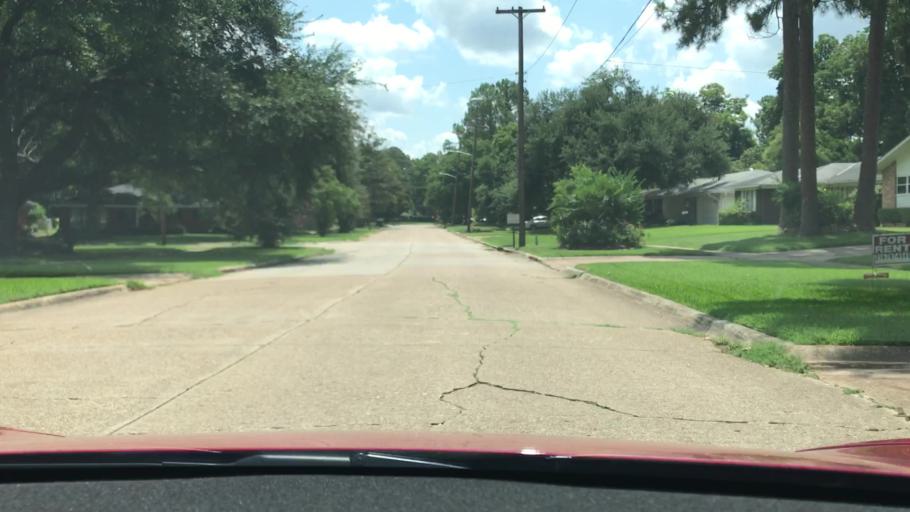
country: US
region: Louisiana
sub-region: Bossier Parish
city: Bossier City
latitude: 32.4576
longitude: -93.7314
